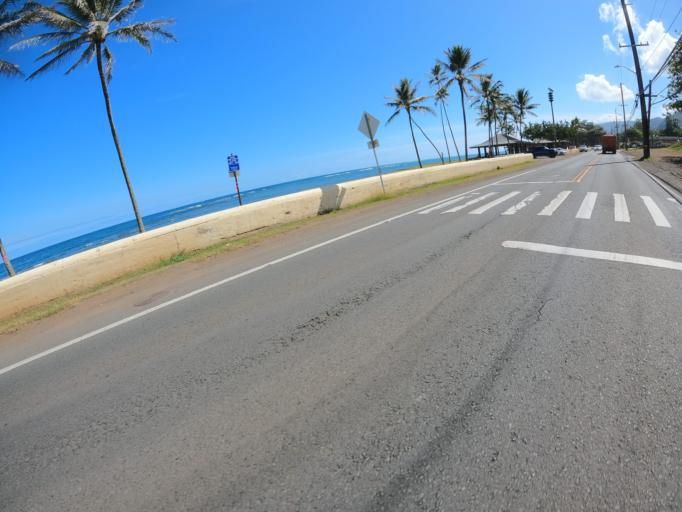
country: US
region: Hawaii
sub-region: Honolulu County
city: Hau'ula
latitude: 21.6132
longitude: -157.9122
